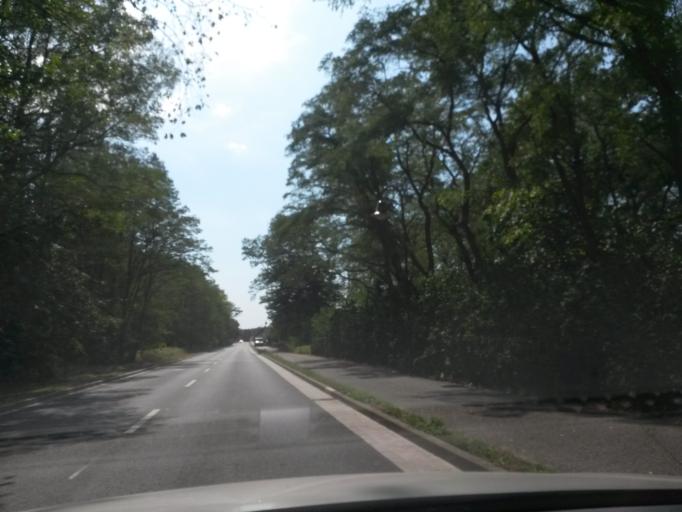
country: DE
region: Saxony-Anhalt
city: Jerichow
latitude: 52.4265
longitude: 11.9965
